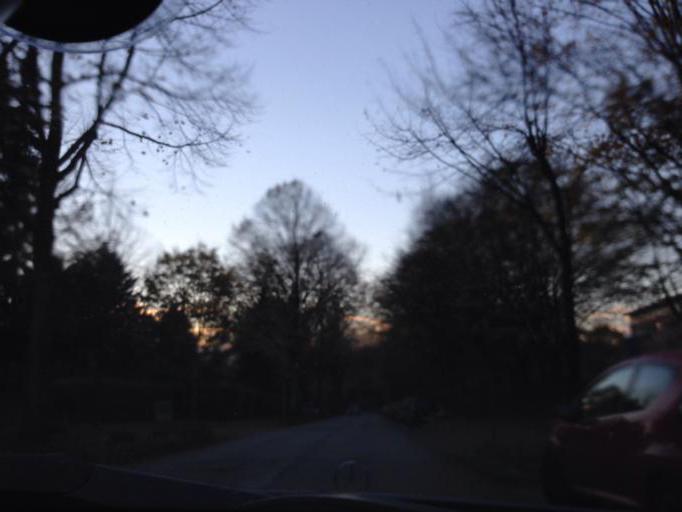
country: DE
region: Hamburg
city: Wandsbek
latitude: 53.5751
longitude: 10.1251
